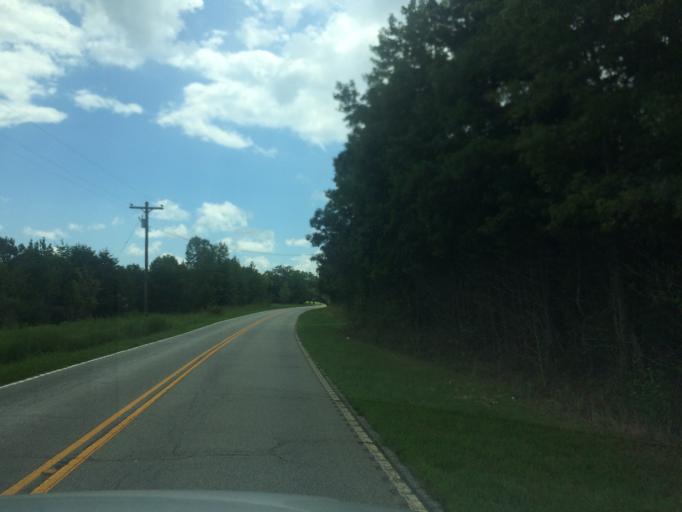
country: US
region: South Carolina
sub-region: Spartanburg County
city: Boiling Springs
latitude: 35.1726
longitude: -82.0297
